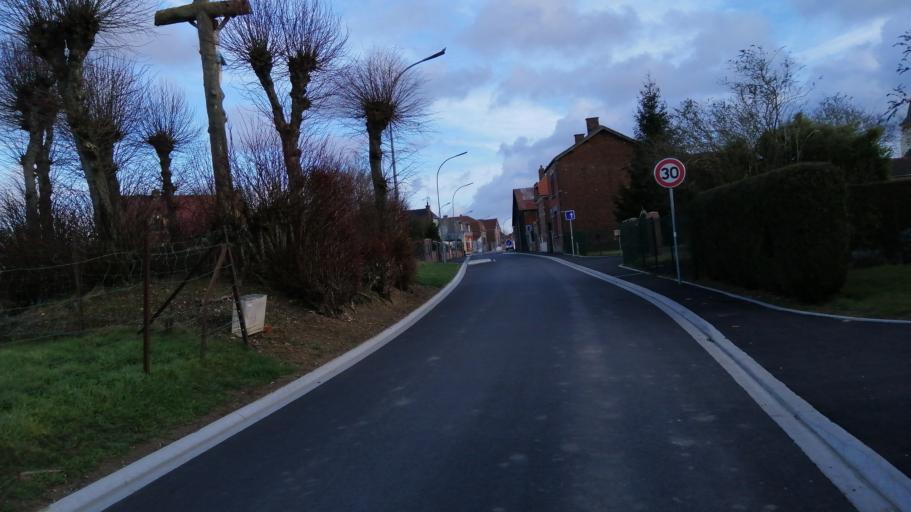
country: FR
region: Nord-Pas-de-Calais
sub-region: Departement du Pas-de-Calais
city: Beaurains
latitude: 50.2364
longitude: 2.7934
